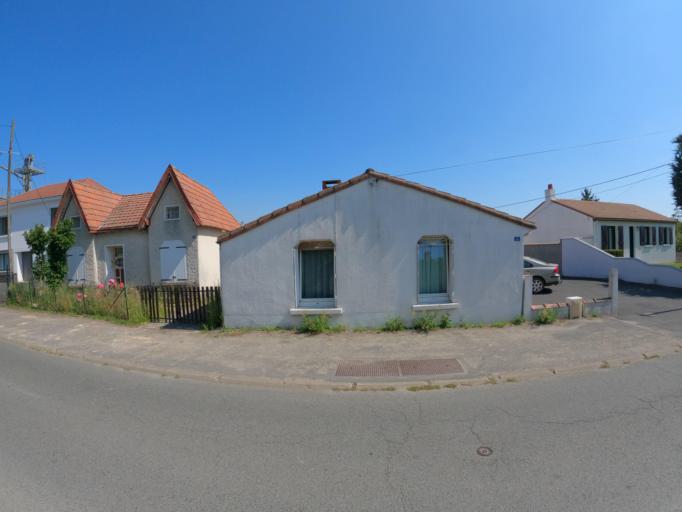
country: FR
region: Pays de la Loire
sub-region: Departement de la Loire-Atlantique
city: Montbert
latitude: 47.0595
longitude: -1.4903
